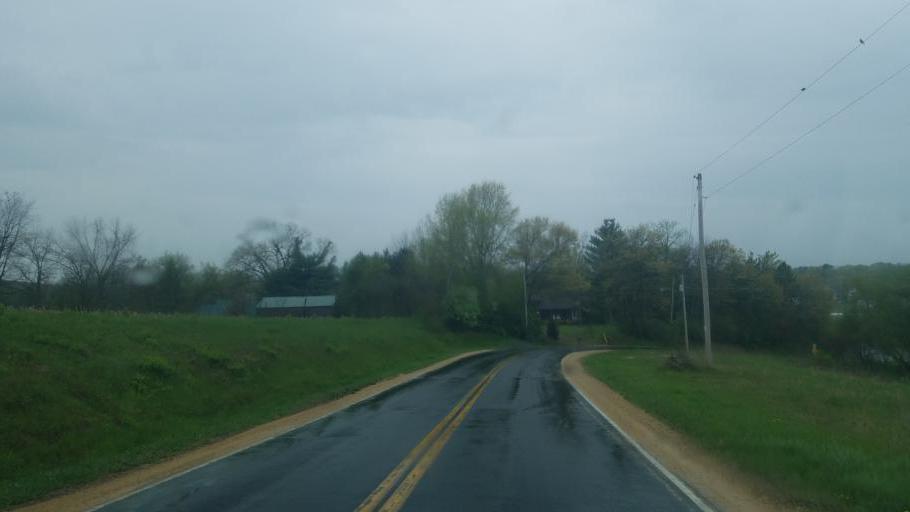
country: US
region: Wisconsin
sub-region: Vernon County
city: Hillsboro
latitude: 43.6511
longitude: -90.3304
